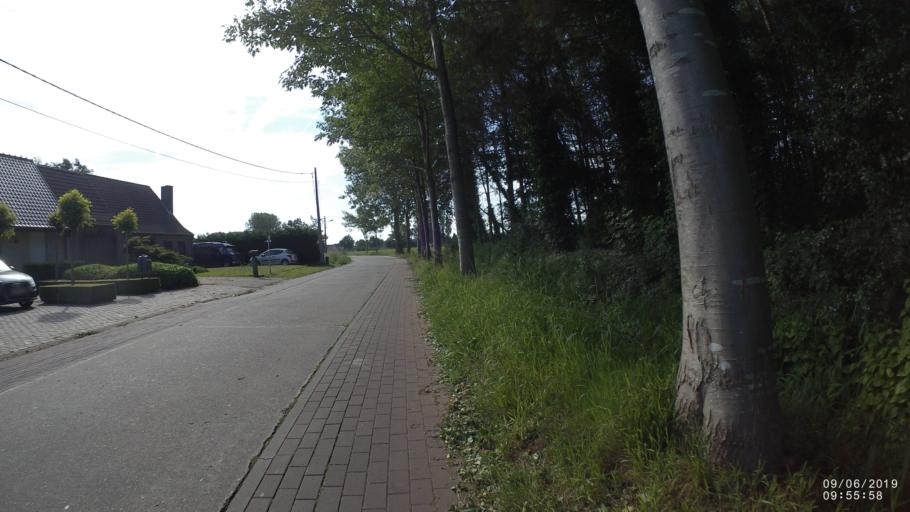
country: BE
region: Flanders
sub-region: Provincie Oost-Vlaanderen
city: Eeklo
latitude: 51.1903
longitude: 3.5035
